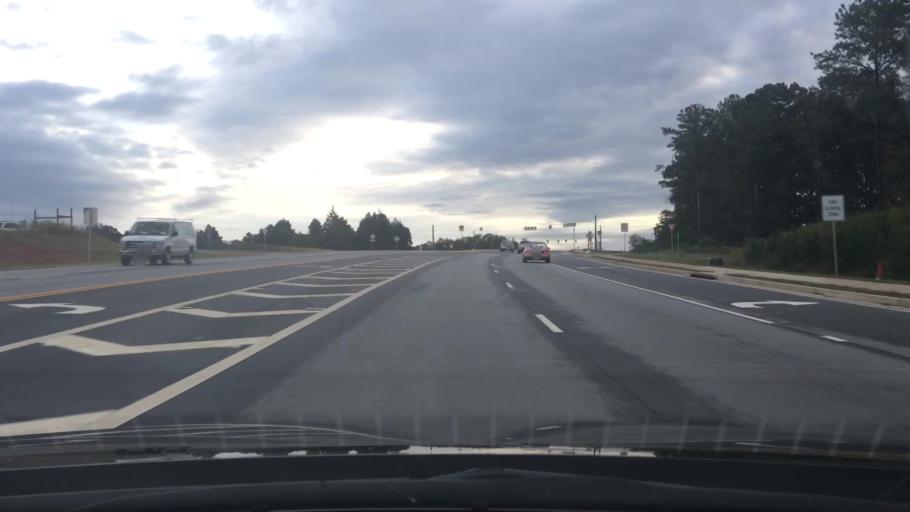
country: US
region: Georgia
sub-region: Spalding County
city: Experiment
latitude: 33.2473
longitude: -84.3008
